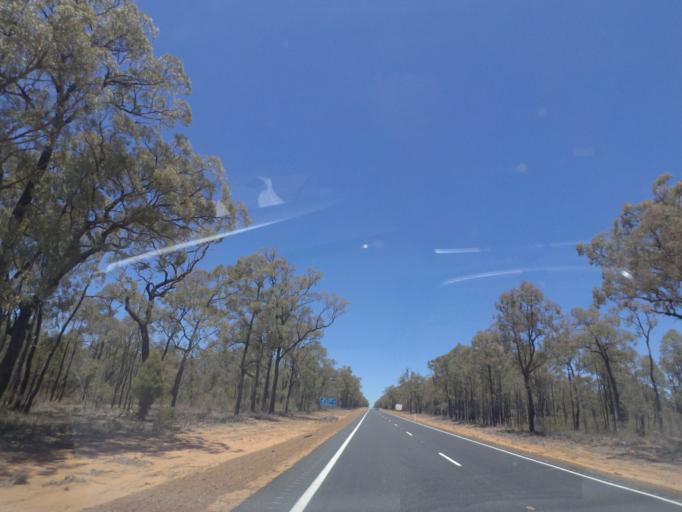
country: AU
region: New South Wales
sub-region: Narrabri
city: Narrabri
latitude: -30.7258
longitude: 149.5231
